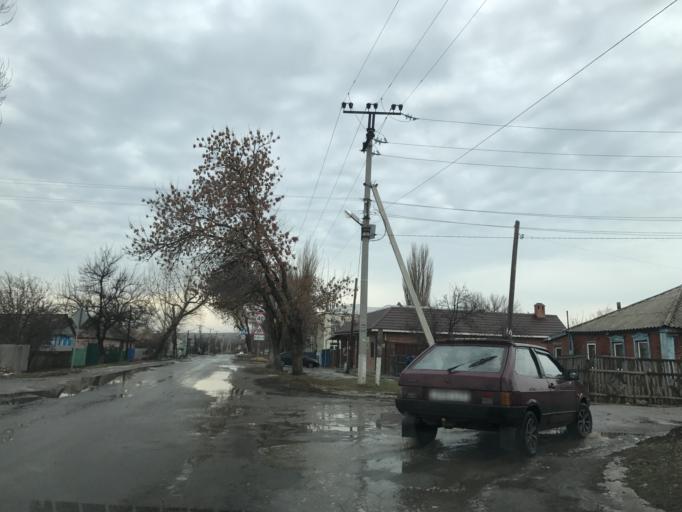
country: RU
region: Rostov
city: Glubokiy
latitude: 48.5224
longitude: 40.3149
